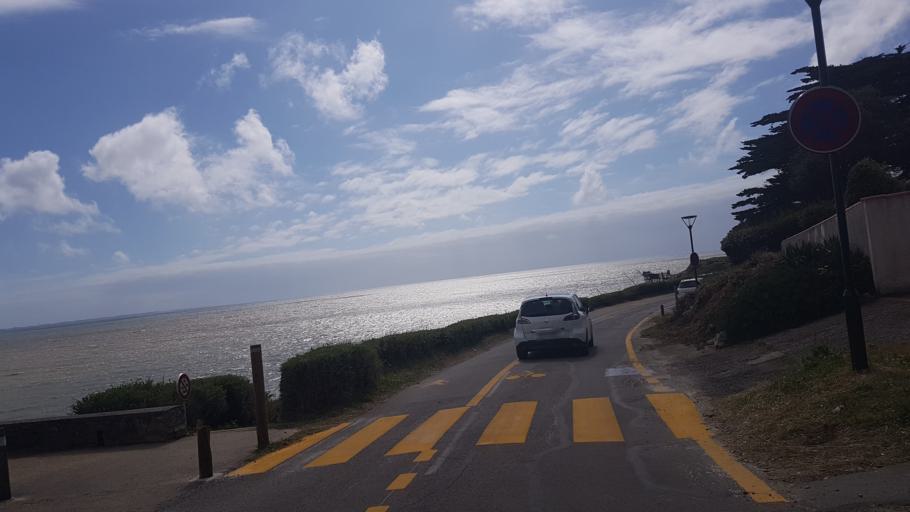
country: FR
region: Pays de la Loire
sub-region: Departement de la Loire-Atlantique
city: Pornic
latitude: 47.1120
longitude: -2.1386
